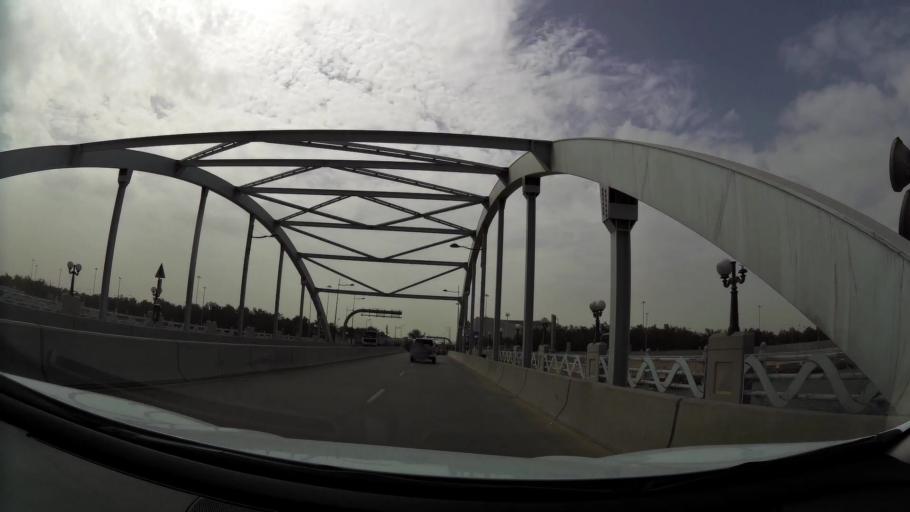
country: AE
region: Abu Dhabi
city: Abu Dhabi
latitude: 24.4008
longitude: 54.5031
